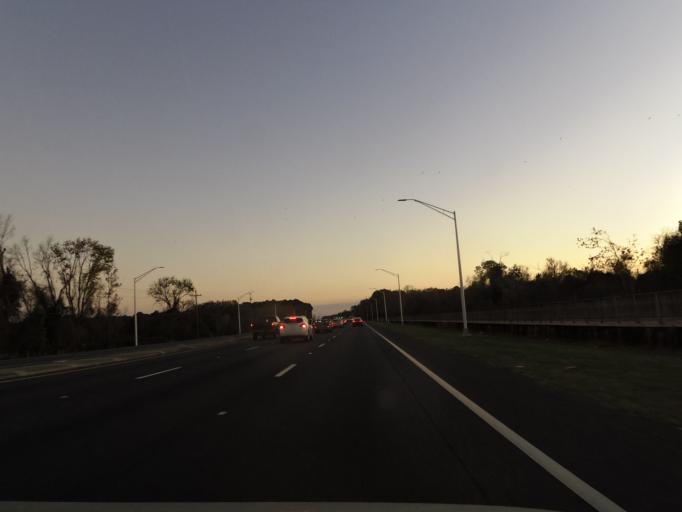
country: US
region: Florida
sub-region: Clay County
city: Orange Park
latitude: 30.1278
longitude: -81.7045
